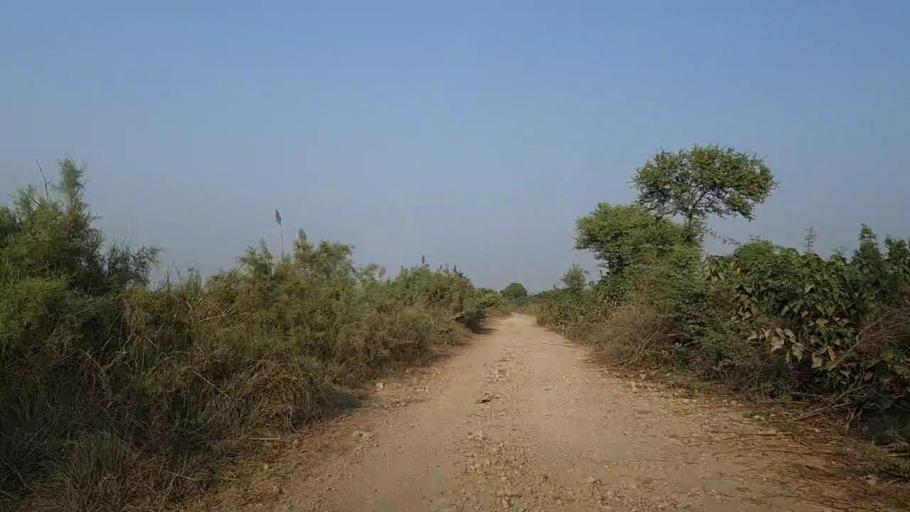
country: PK
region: Sindh
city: Thatta
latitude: 24.6822
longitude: 67.7868
